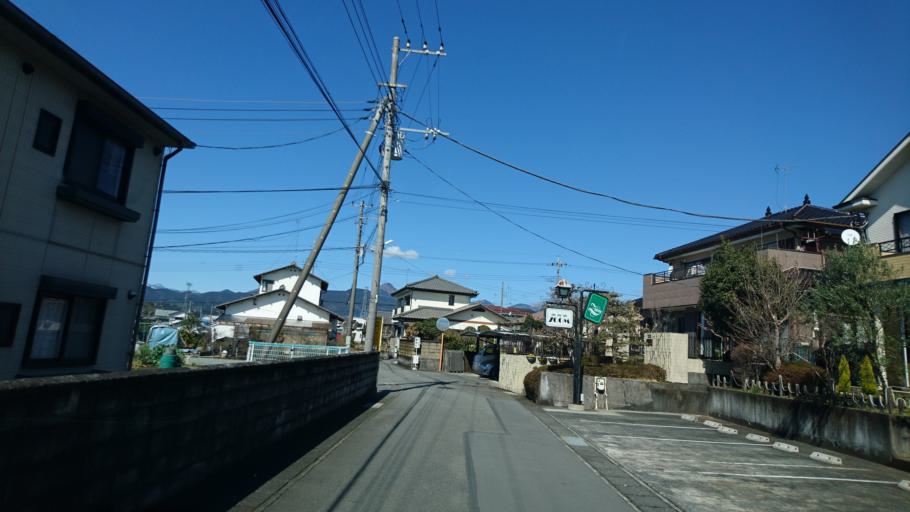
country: JP
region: Shizuoka
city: Fujinomiya
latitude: 35.2485
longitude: 138.6143
